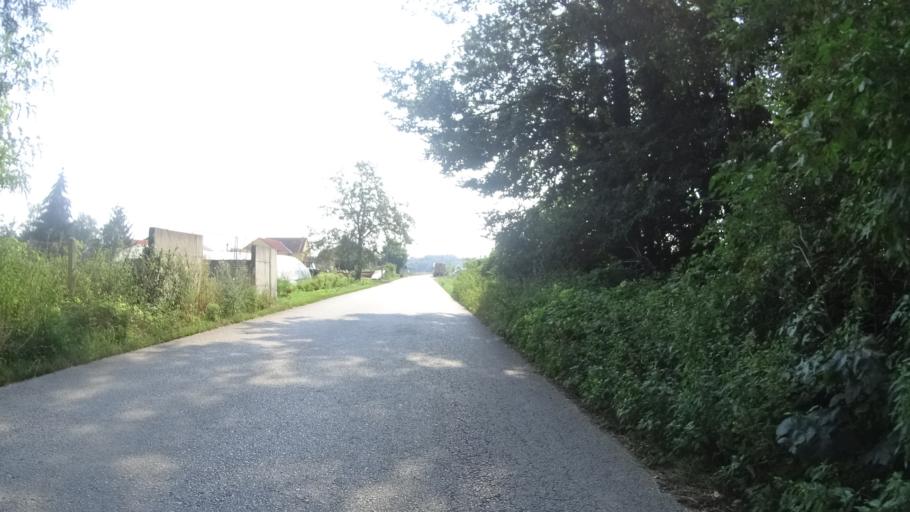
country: HR
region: Medimurska
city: Belica
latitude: 46.3956
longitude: 16.5205
